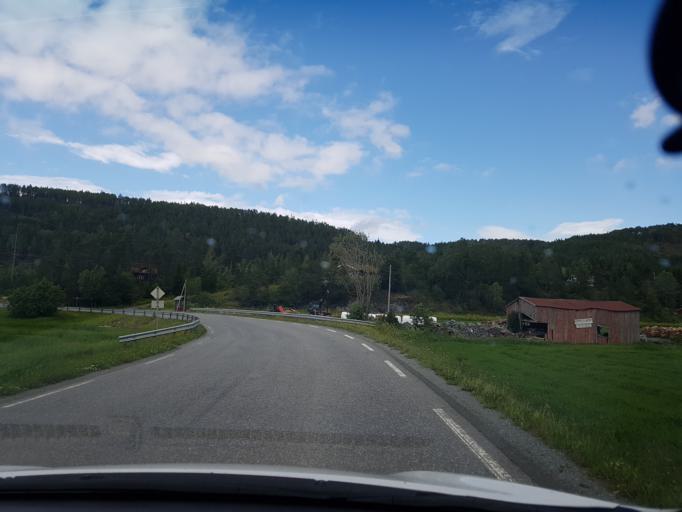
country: NO
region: Nord-Trondelag
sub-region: Stjordal
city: Stjordalshalsen
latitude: 63.6126
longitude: 10.9365
